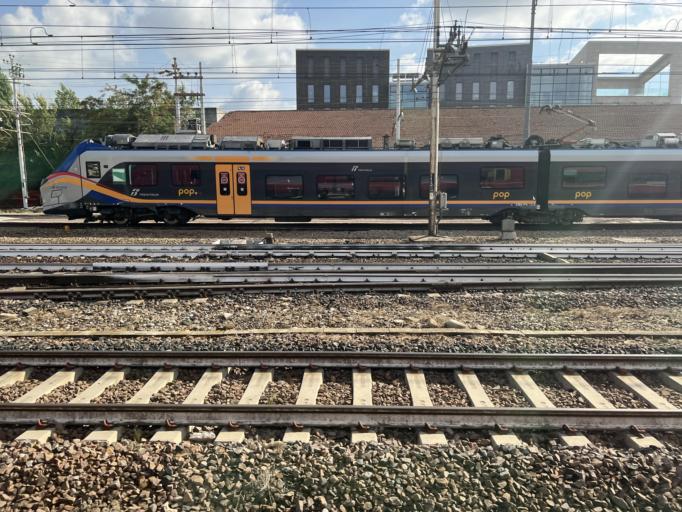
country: IT
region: Emilia-Romagna
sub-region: Provincia di Parma
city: Parma
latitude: 44.8085
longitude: 10.3353
